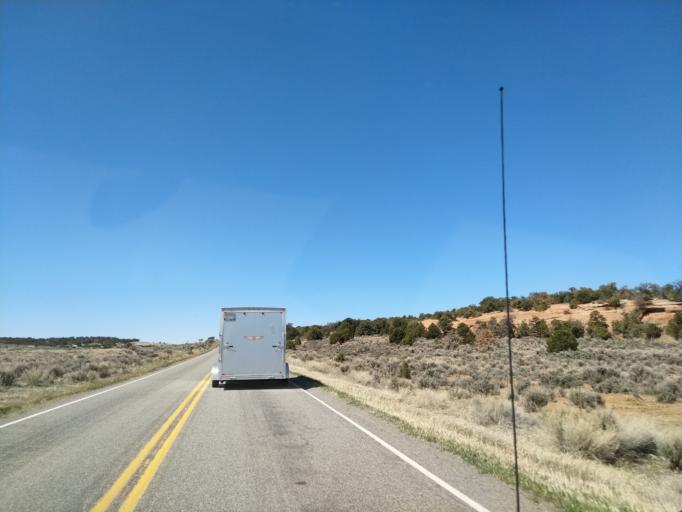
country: US
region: Colorado
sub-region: Mesa County
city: Redlands
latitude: 39.0051
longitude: -108.6932
